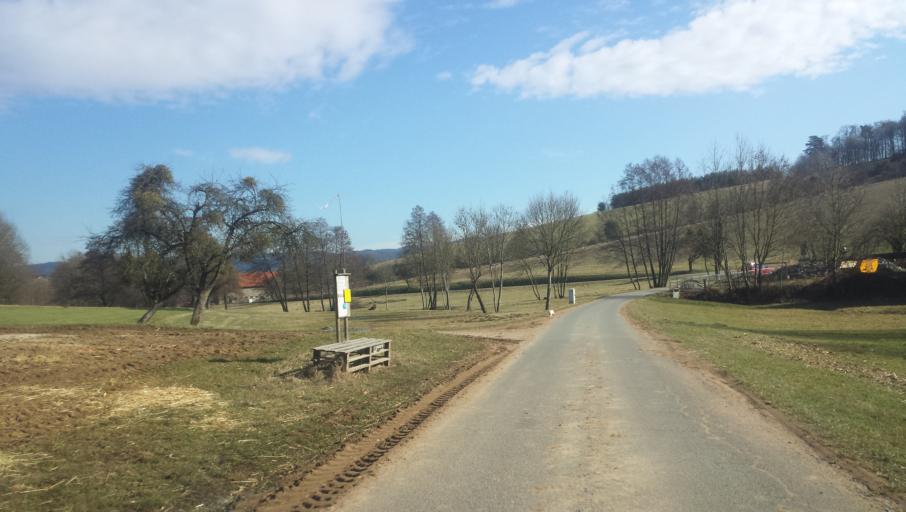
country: DE
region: Hesse
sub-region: Regierungsbezirk Darmstadt
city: Frankisch-Crumbach
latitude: 49.7421
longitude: 8.8338
